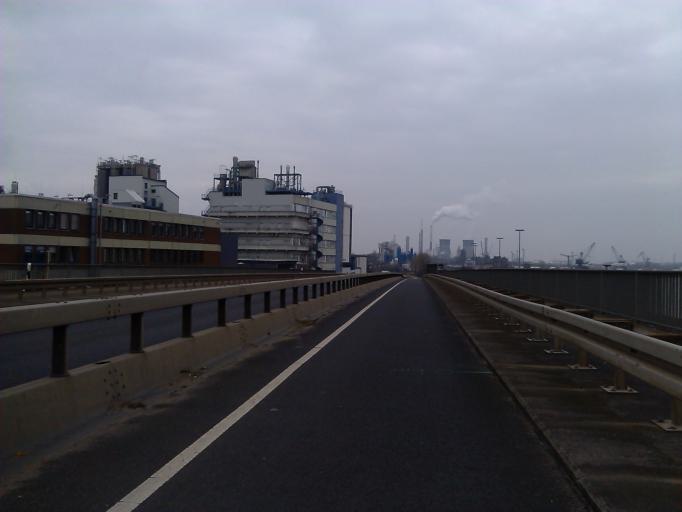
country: DE
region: North Rhine-Westphalia
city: Wesseling
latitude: 50.8371
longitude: 6.9760
